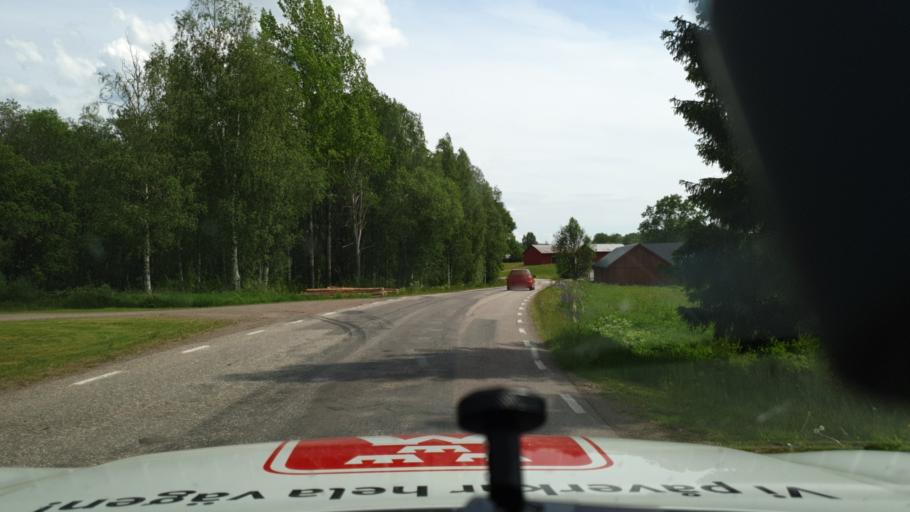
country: SE
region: Vaermland
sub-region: Torsby Kommun
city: Torsby
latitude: 59.9876
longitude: 12.8594
